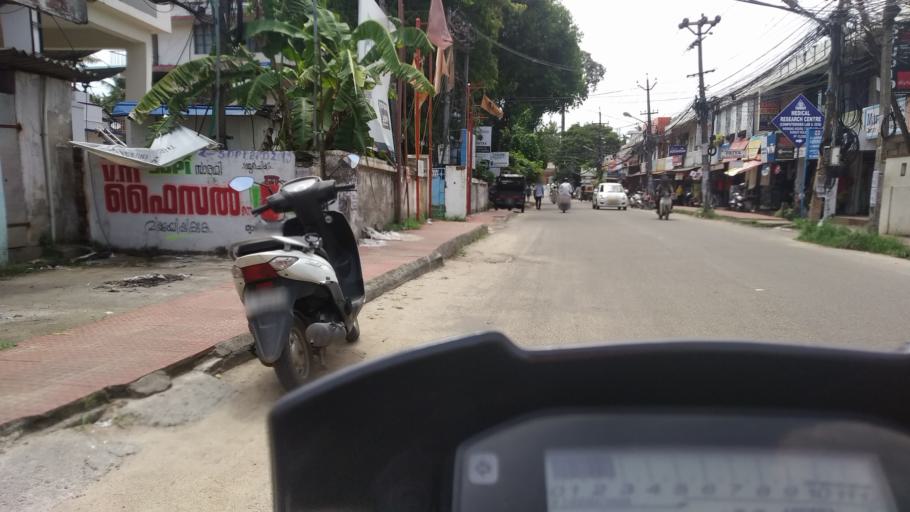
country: IN
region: Kerala
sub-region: Ernakulam
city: Cochin
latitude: 9.9919
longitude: 76.3090
